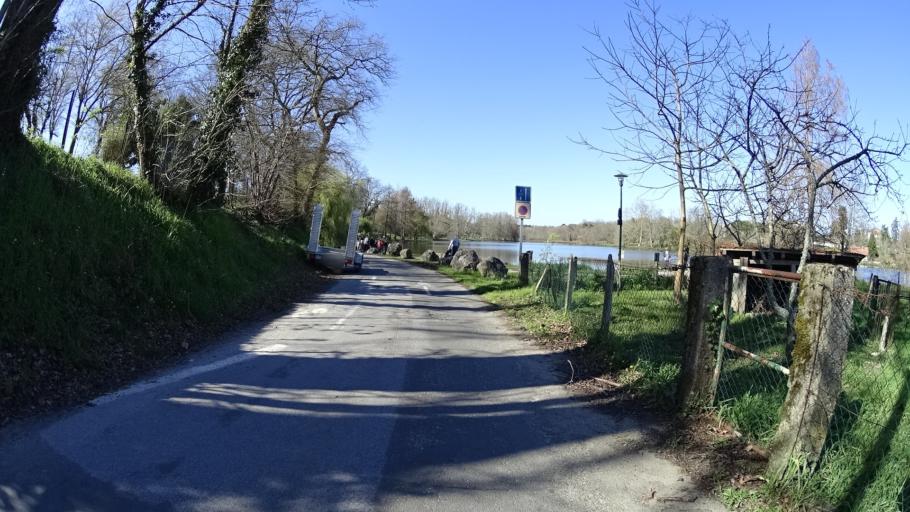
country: FR
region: Aquitaine
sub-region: Departement des Landes
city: Saint-Paul-les-Dax
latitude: 43.7276
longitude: -1.0689
